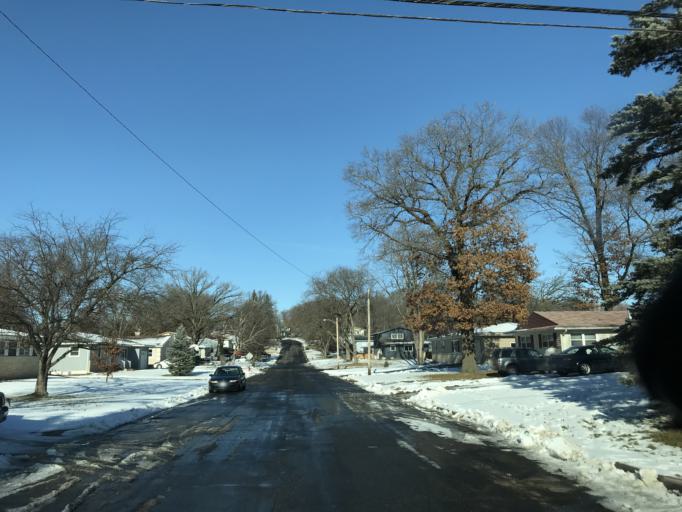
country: US
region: Wisconsin
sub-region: Dane County
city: Monona
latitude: 43.0483
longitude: -89.3276
